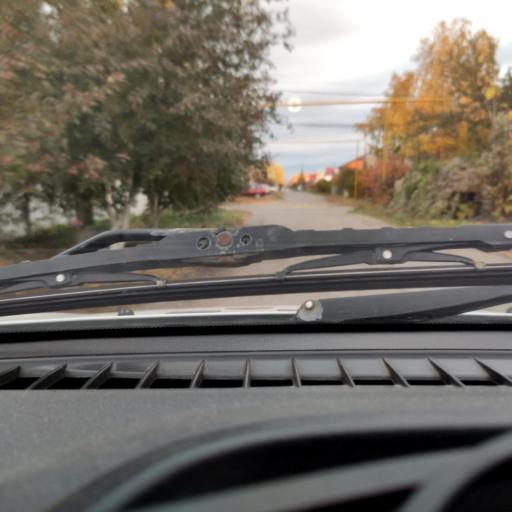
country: RU
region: Samara
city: Tol'yatti
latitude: 53.5361
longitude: 49.4208
